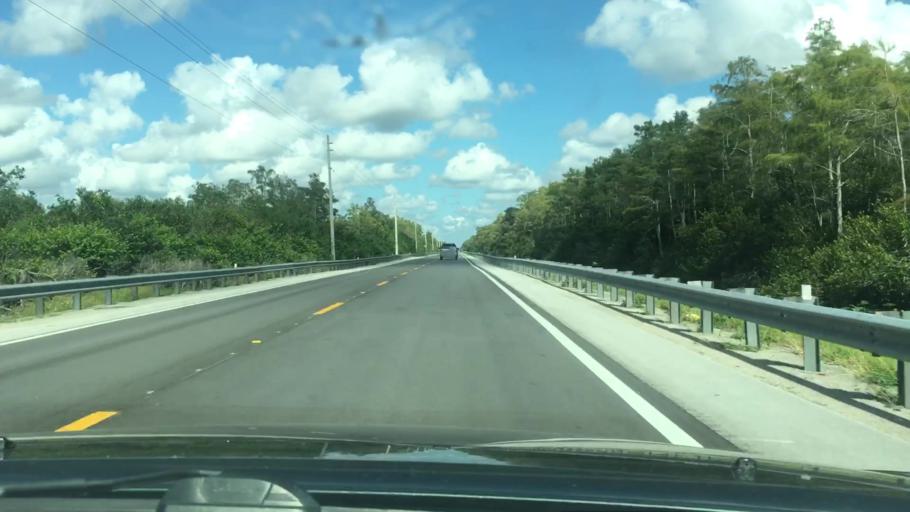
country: US
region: Florida
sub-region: Miami-Dade County
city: Kendall West
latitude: 25.7660
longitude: -80.8325
